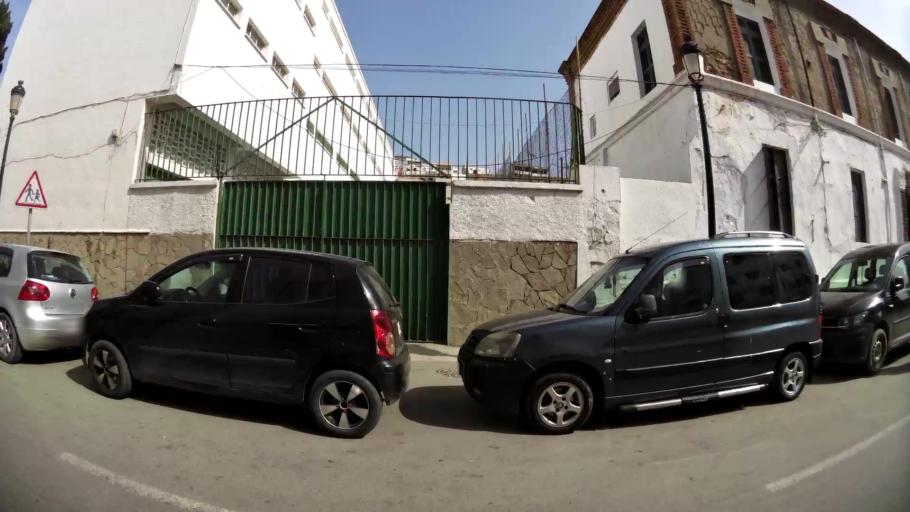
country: MA
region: Tanger-Tetouan
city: Tetouan
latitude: 35.5727
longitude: -5.3770
